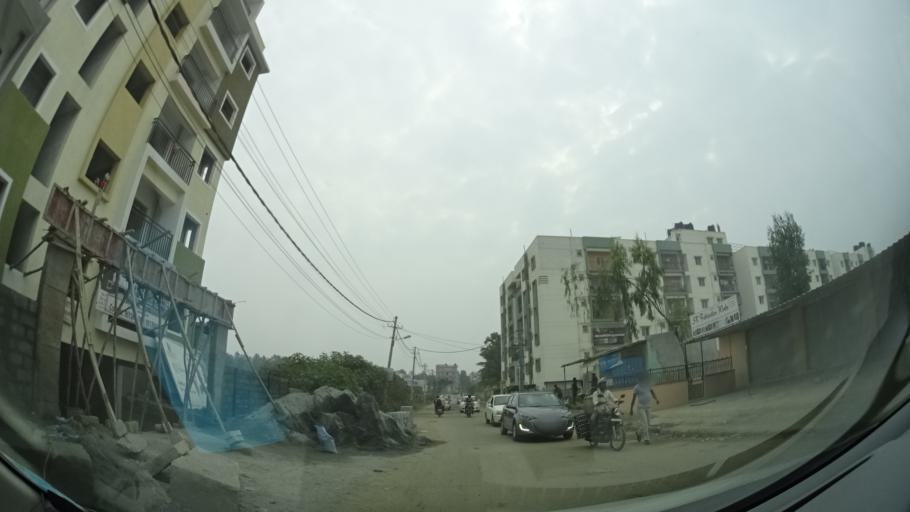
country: IN
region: Karnataka
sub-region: Bangalore Rural
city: Hoskote
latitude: 12.9778
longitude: 77.7371
